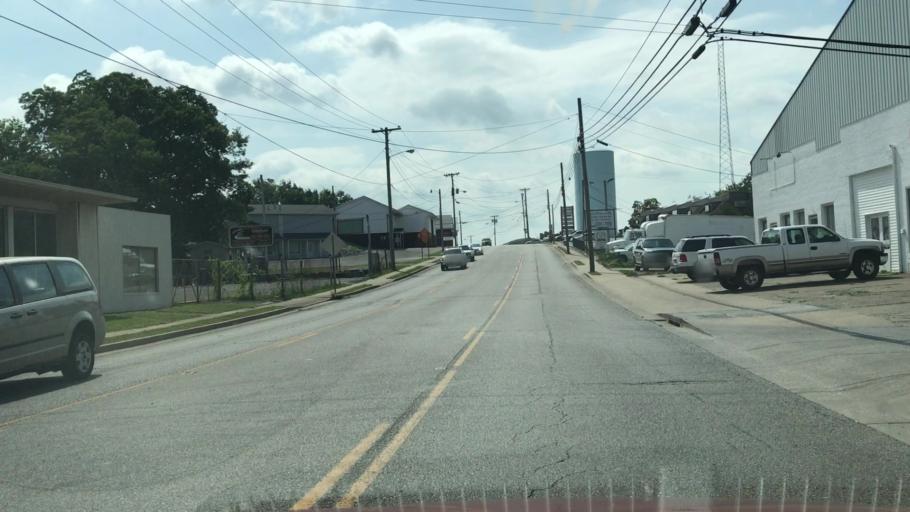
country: US
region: Kentucky
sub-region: Barren County
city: Glasgow
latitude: 37.0008
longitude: -85.9244
